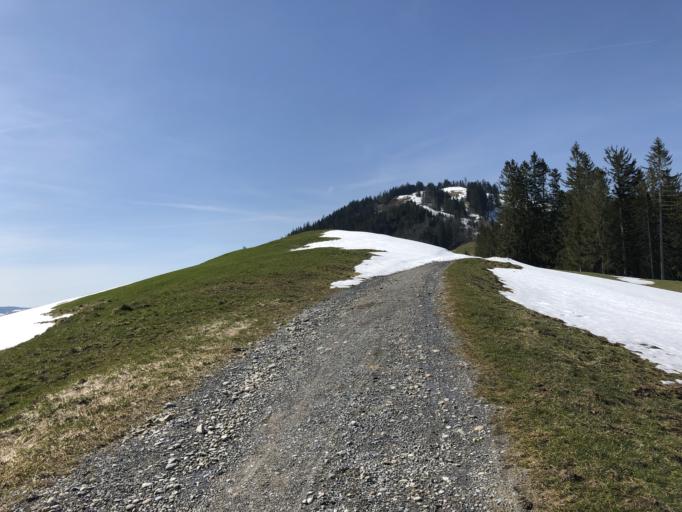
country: CH
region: Appenzell Innerrhoden
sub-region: Appenzell Inner Rhodes
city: Gonten
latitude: 47.3416
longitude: 9.3512
